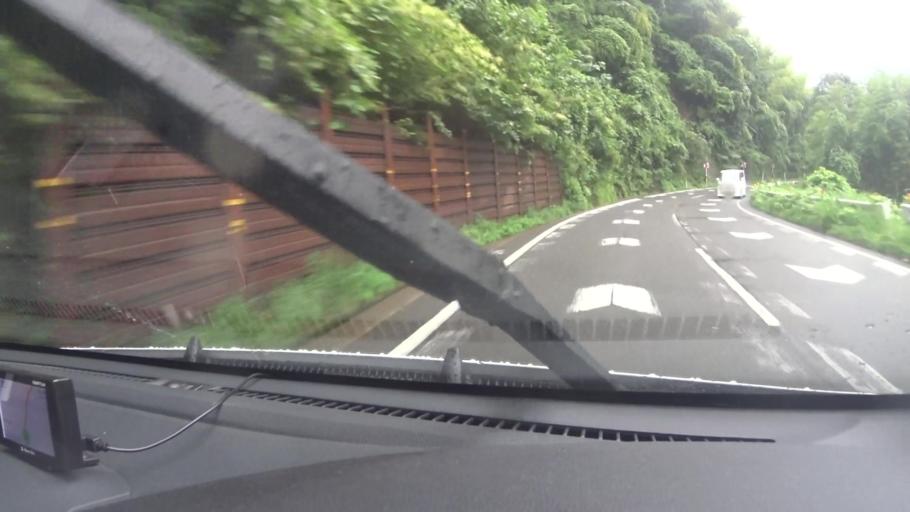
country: JP
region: Kyoto
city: Ayabe
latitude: 35.2564
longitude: 135.2771
